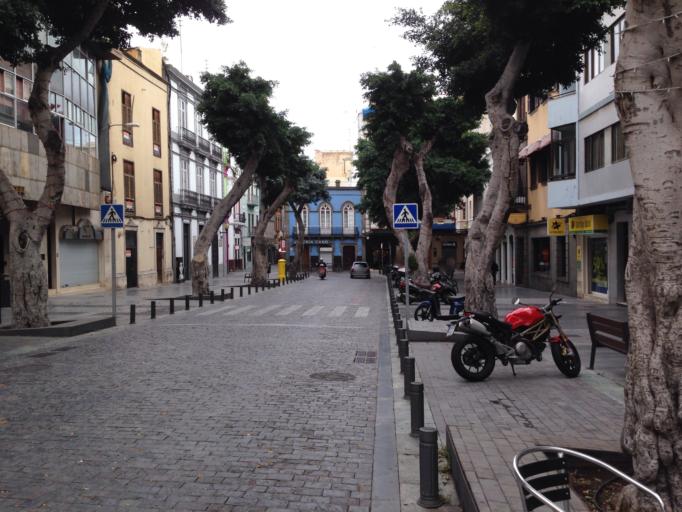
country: ES
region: Canary Islands
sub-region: Provincia de Las Palmas
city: Las Palmas de Gran Canaria
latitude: 28.1054
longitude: -15.4179
